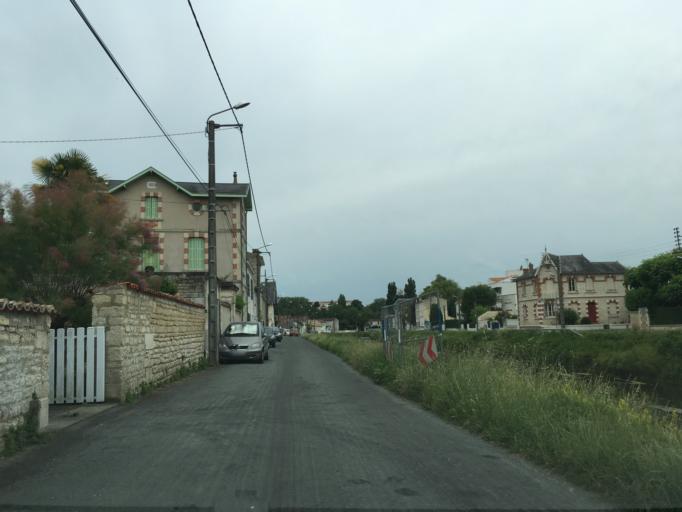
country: FR
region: Poitou-Charentes
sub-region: Departement des Deux-Sevres
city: Niort
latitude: 46.3251
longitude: -0.4714
